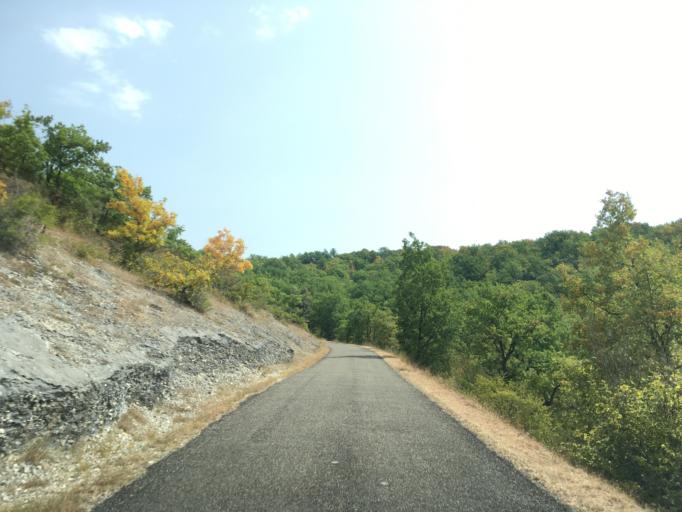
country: FR
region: Midi-Pyrenees
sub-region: Departement du Lot
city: Le Vigan
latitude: 44.7606
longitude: 1.5492
